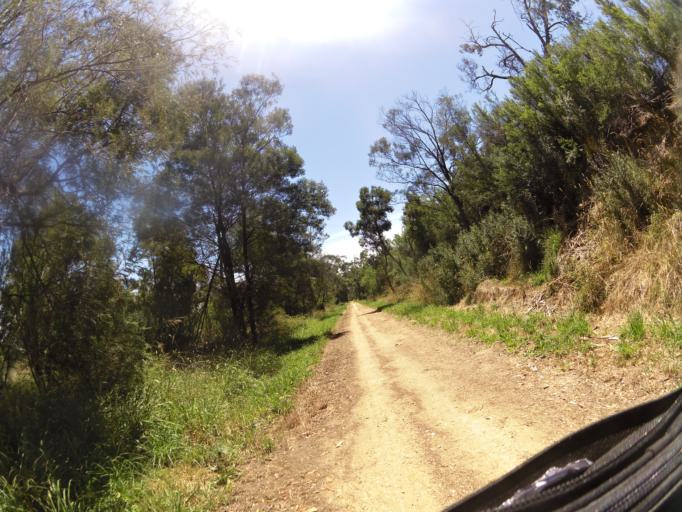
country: AU
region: Victoria
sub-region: East Gippsland
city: Lakes Entrance
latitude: -37.7185
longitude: 147.8432
